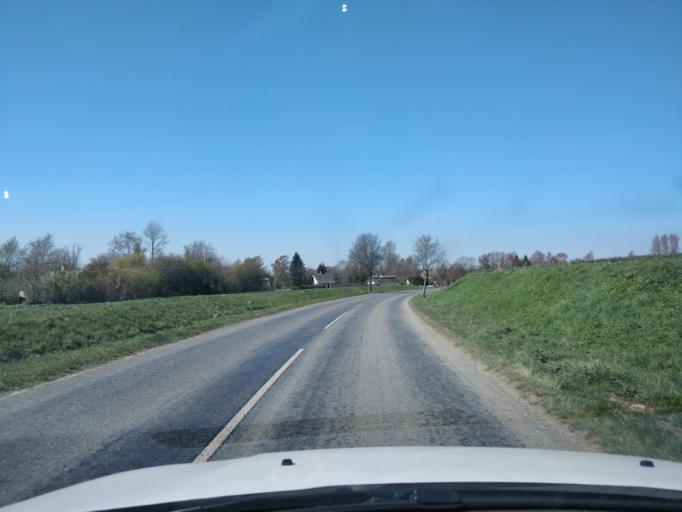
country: DK
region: Zealand
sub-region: Vordingborg Kommune
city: Stege
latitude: 54.9867
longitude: 12.3865
